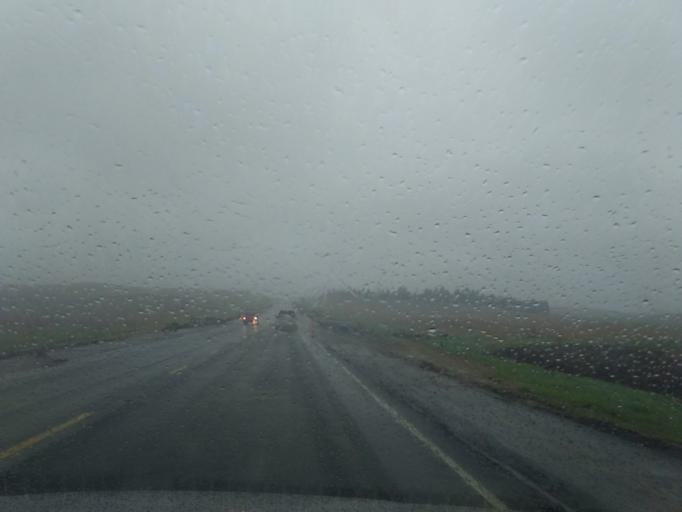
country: US
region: Nebraska
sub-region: Wayne County
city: Wayne
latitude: 42.1755
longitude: -97.1864
